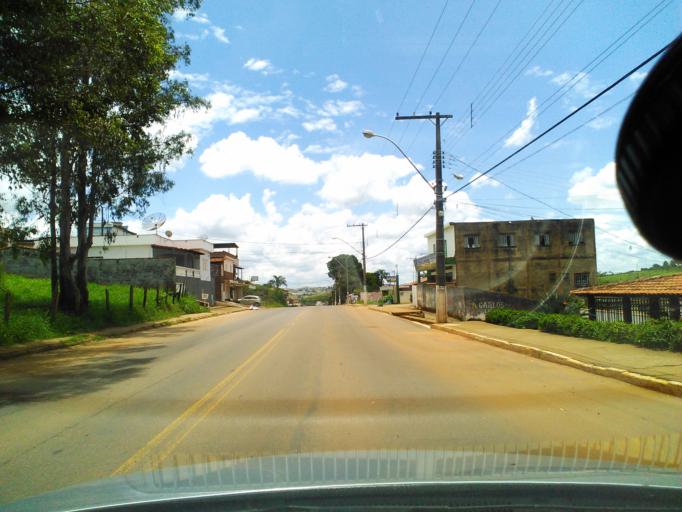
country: BR
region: Minas Gerais
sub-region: Tres Coracoes
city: Tres Coracoes
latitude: -21.7248
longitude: -45.2628
